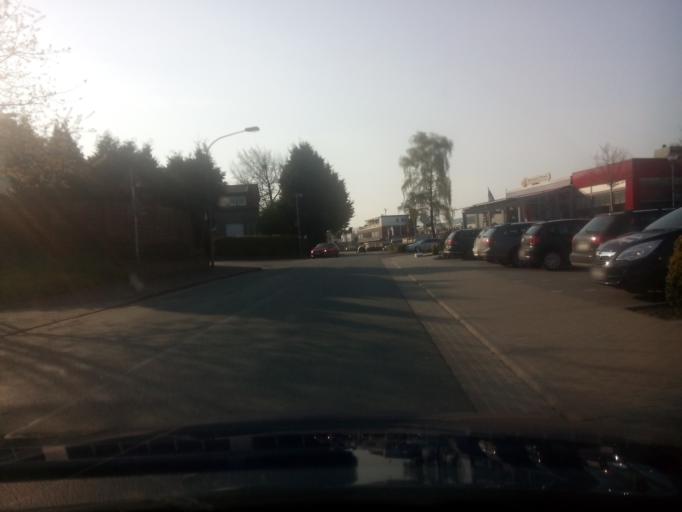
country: DE
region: Lower Saxony
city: Ritterhude
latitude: 53.1853
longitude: 8.7546
